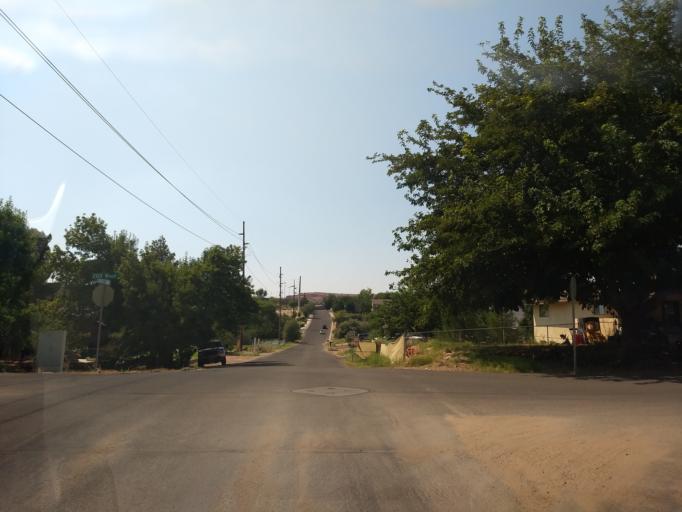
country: US
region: Utah
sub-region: Washington County
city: Washington
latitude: 37.1278
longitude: -113.5131
